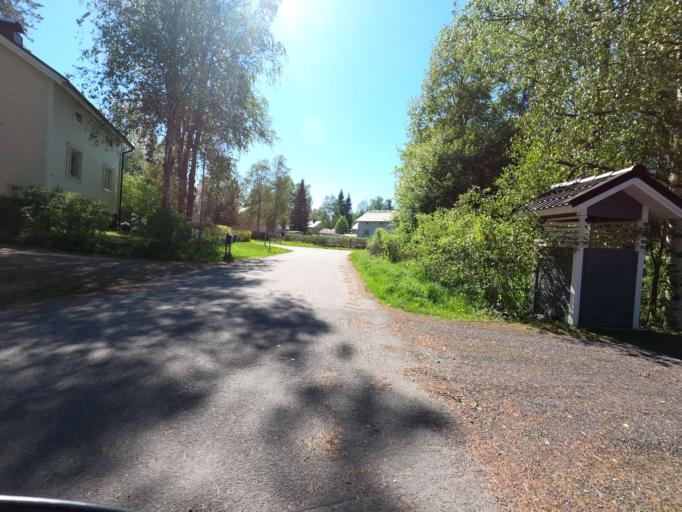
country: FI
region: North Karelia
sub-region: Joensuu
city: Joensuu
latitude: 62.5994
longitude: 29.8189
